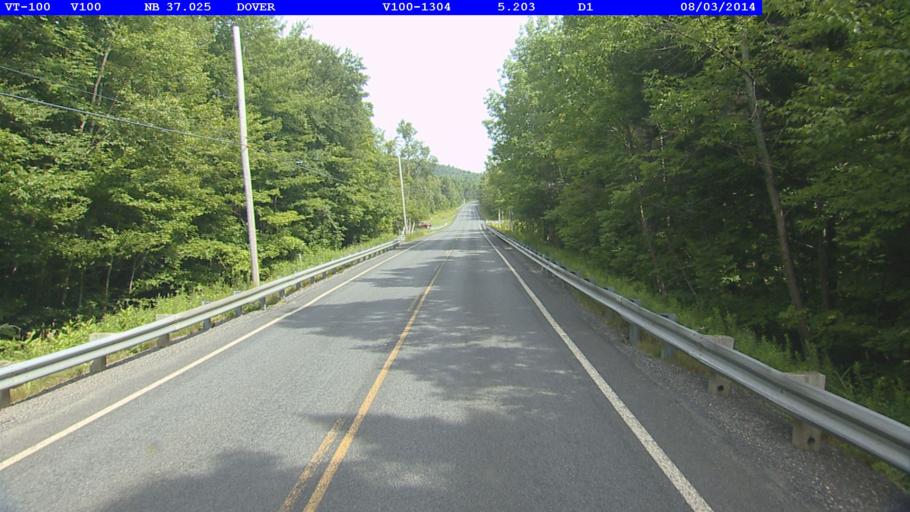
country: US
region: Vermont
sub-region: Windham County
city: Dover
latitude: 42.9864
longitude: -72.8890
